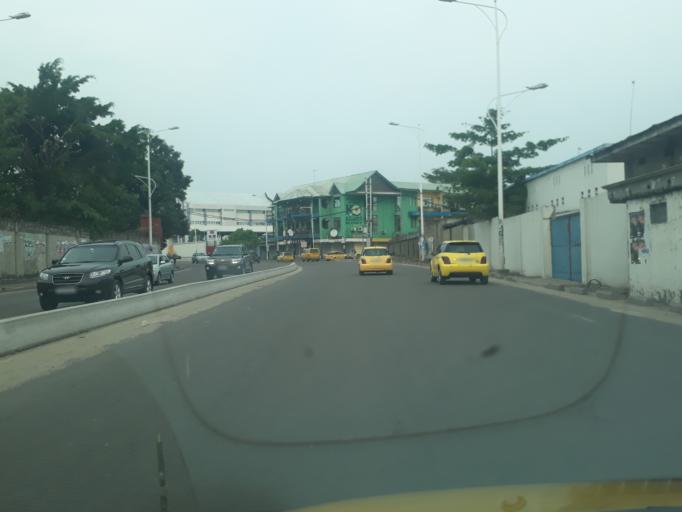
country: CD
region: Kinshasa
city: Kinshasa
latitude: -4.3332
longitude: 15.2610
